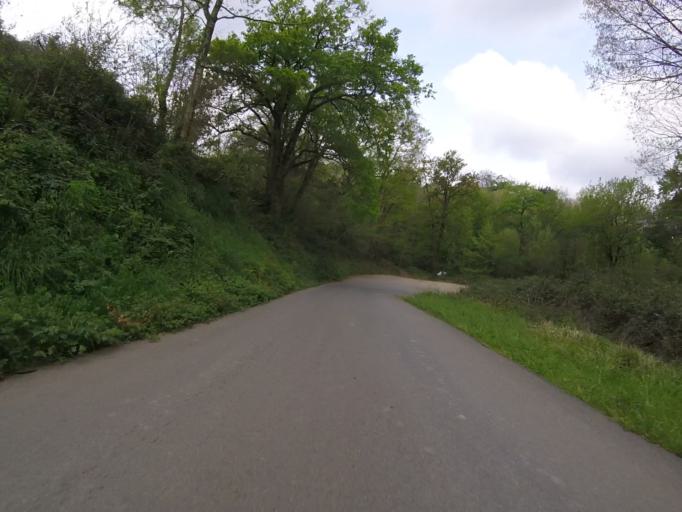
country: ES
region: Basque Country
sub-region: Provincia de Guipuzcoa
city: Asteasu
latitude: 43.1817
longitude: -2.0838
